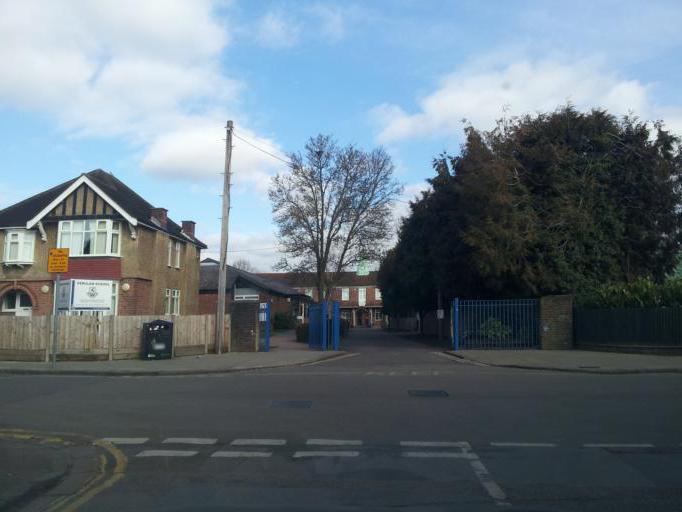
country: GB
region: England
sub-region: Hertfordshire
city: St Albans
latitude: 51.7543
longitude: -0.3161
